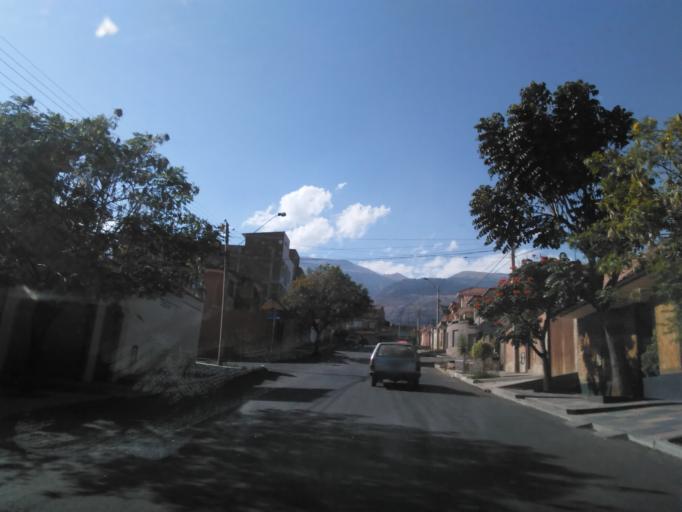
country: BO
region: Cochabamba
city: Cochabamba
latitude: -17.3558
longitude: -66.1649
